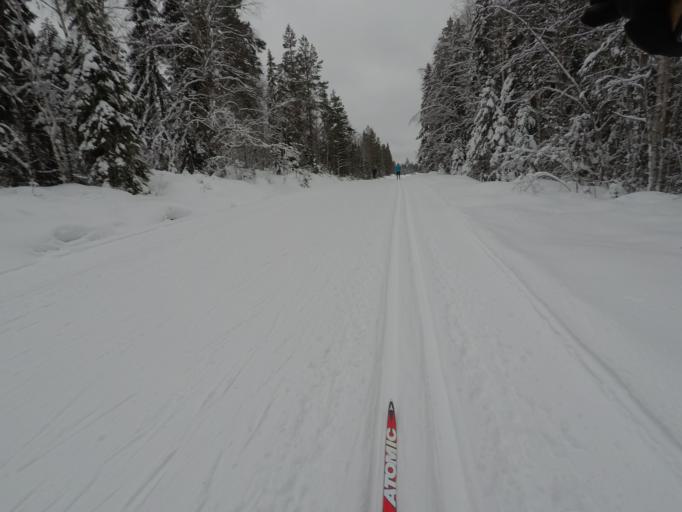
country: SE
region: Dalarna
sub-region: Ludvika Kommun
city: Abborrberget
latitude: 60.1524
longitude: 14.4895
